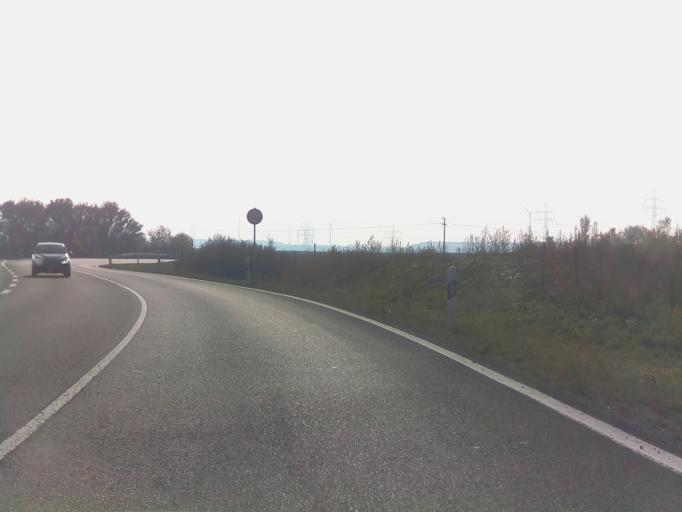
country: DE
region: Bavaria
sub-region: Regierungsbezirk Unterfranken
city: Biebelried
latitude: 49.7757
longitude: 10.0620
